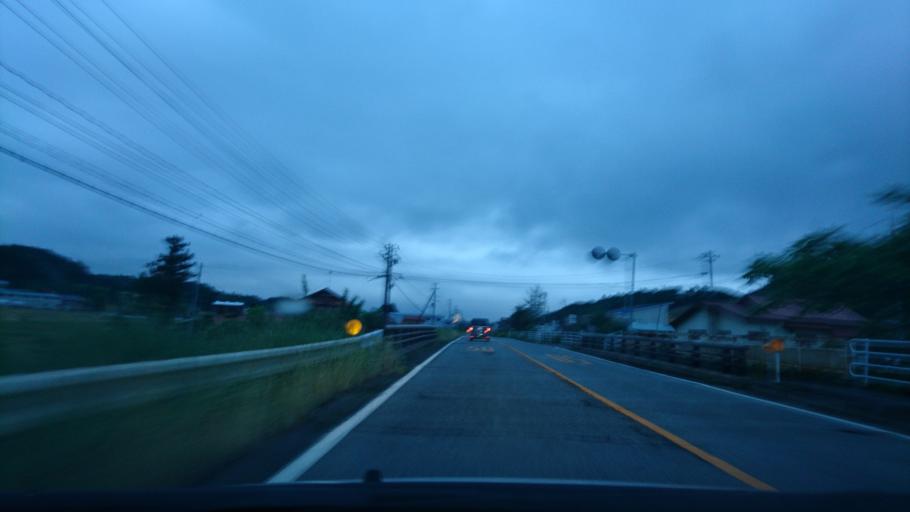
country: JP
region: Iwate
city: Ichinoseki
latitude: 38.8271
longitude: 141.0809
